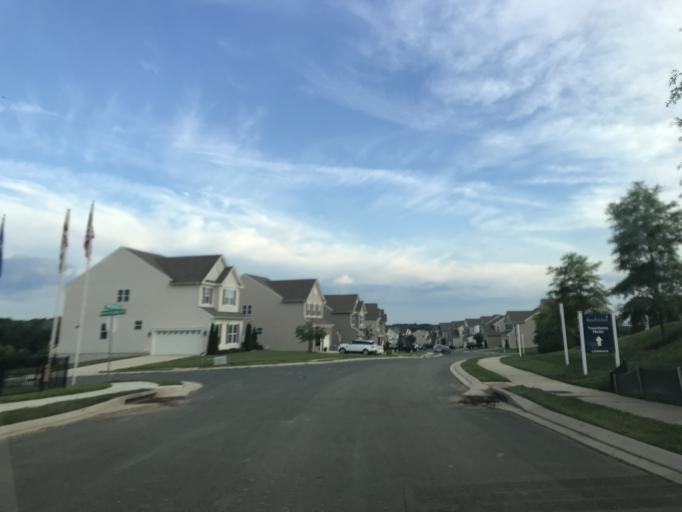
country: US
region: Maryland
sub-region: Harford County
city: Perryman
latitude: 39.5006
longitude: -76.2068
